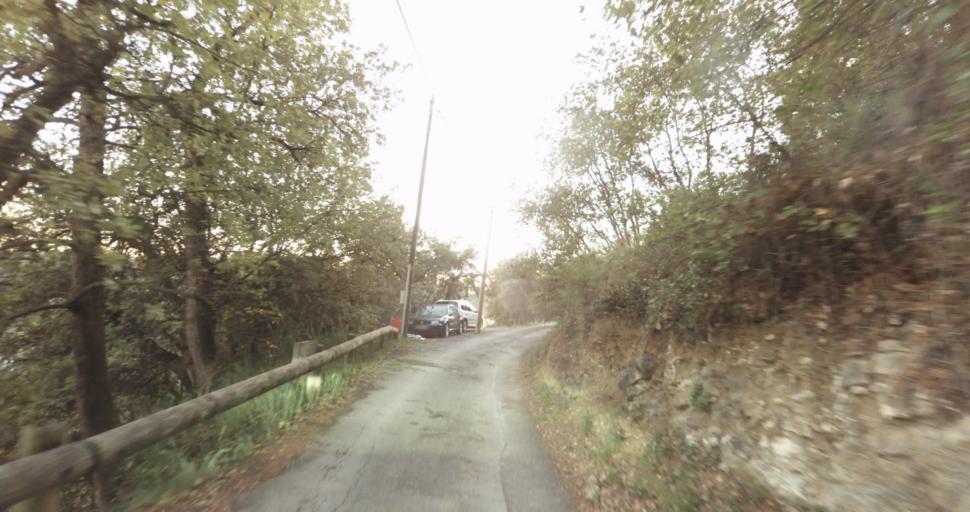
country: FR
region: Provence-Alpes-Cote d'Azur
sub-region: Departement des Alpes-Maritimes
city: La Gaude
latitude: 43.7217
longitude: 7.1364
